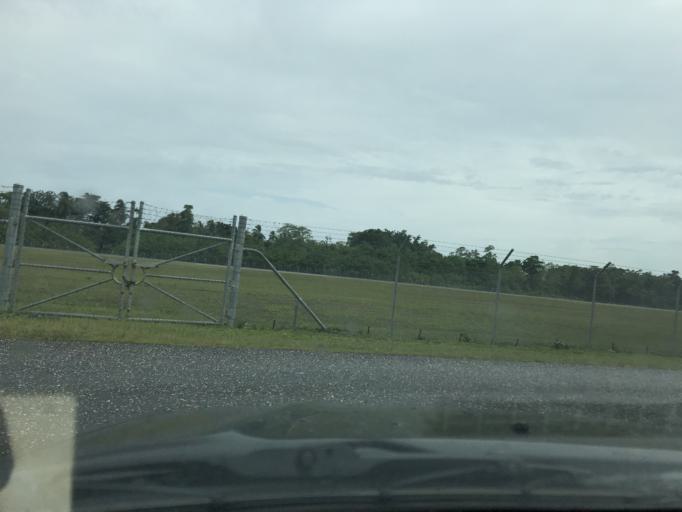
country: SB
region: Western Province
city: Gizo
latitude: -8.3268
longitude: 157.2592
